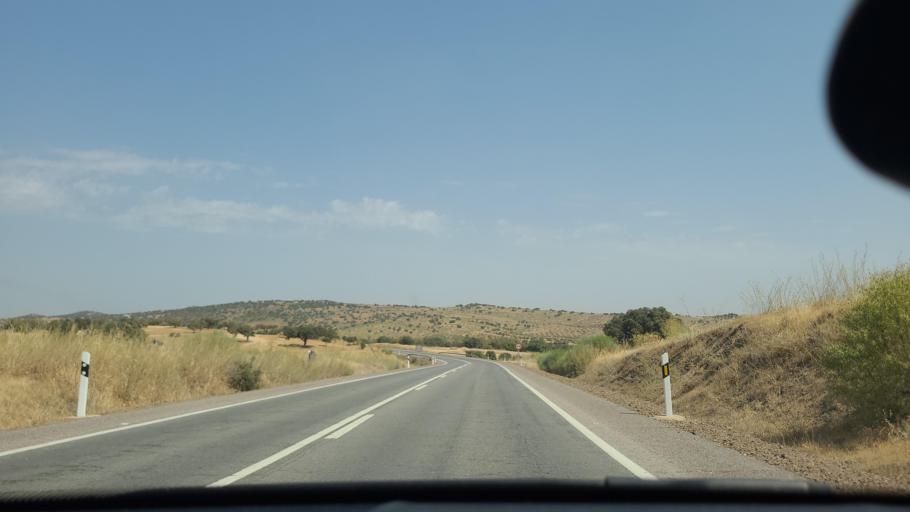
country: ES
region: Extremadura
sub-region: Provincia de Badajoz
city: Feria
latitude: 38.5293
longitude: -6.5404
